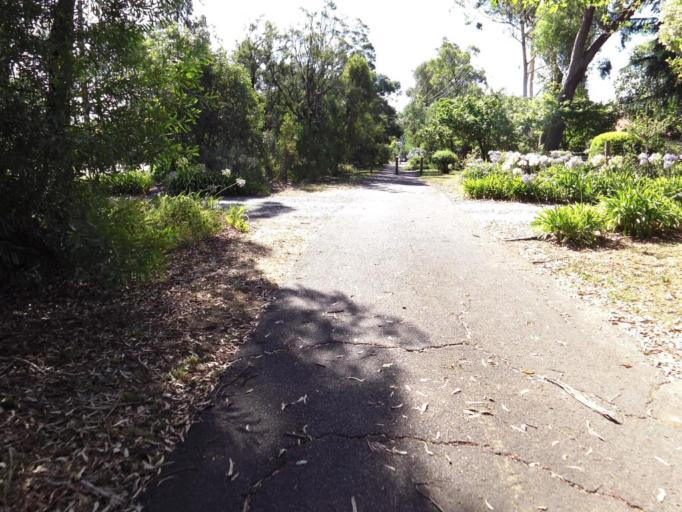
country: AU
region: Victoria
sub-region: Yarra Ranges
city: Kilsyth
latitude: -37.7919
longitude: 145.3152
